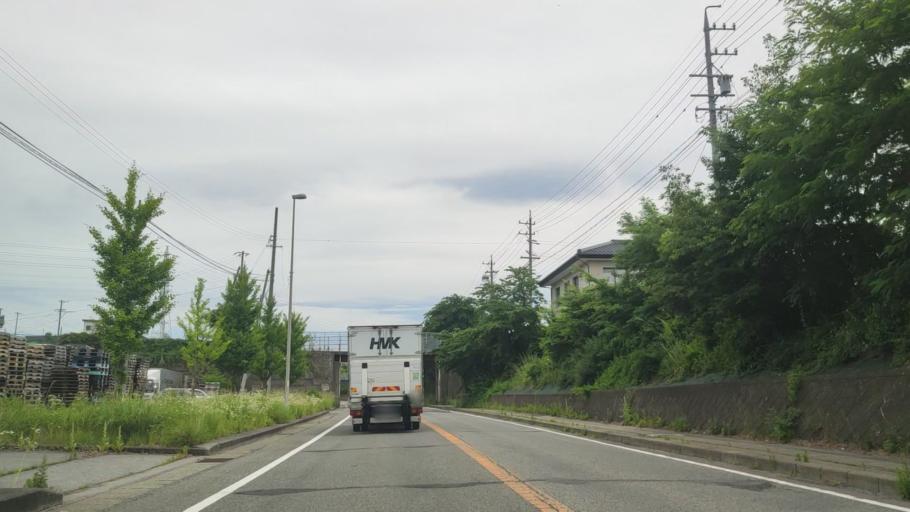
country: JP
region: Nagano
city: Komoro
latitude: 36.3147
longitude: 138.4465
